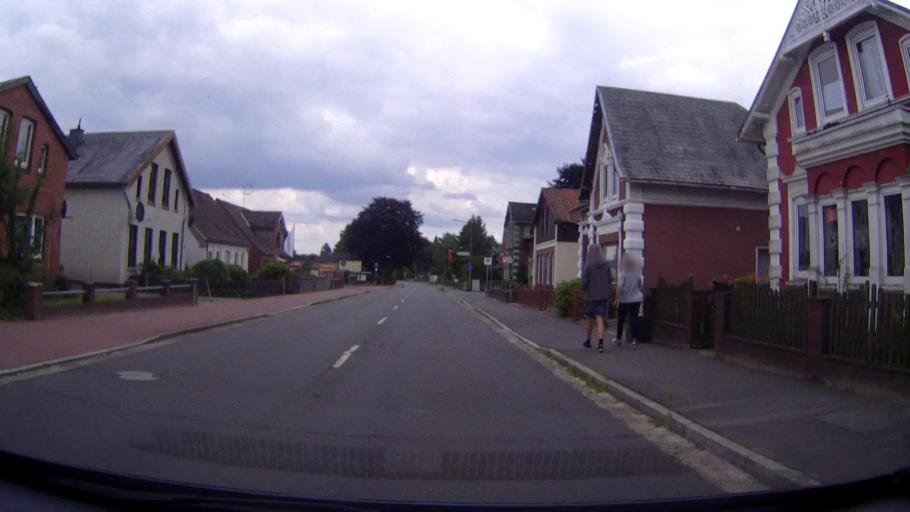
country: DE
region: Schleswig-Holstein
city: Hanerau-Hademarschen
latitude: 54.1240
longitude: 9.4216
